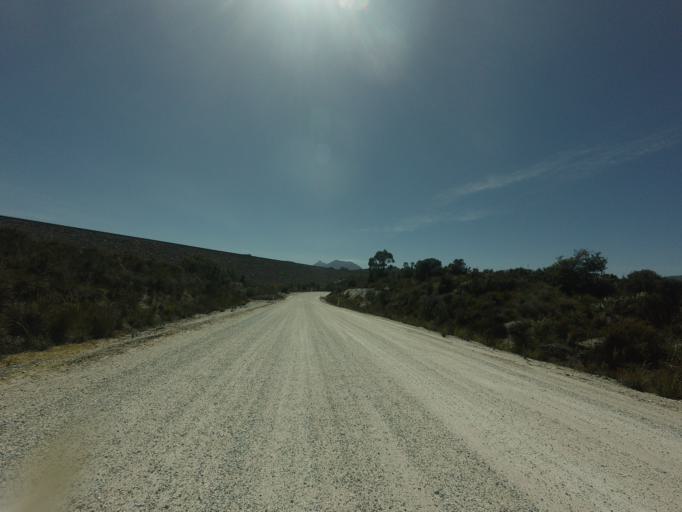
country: AU
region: Tasmania
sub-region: Huon Valley
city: Geeveston
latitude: -43.0327
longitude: 146.2942
